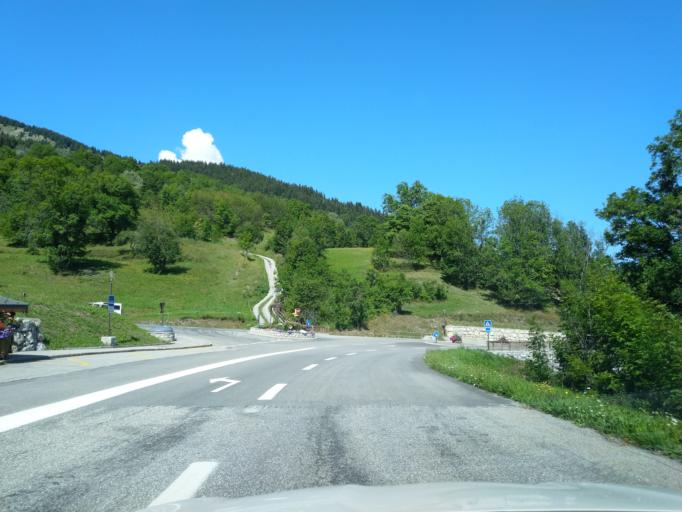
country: FR
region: Rhone-Alpes
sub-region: Departement de la Savoie
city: Les Allues
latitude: 45.4209
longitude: 6.5541
